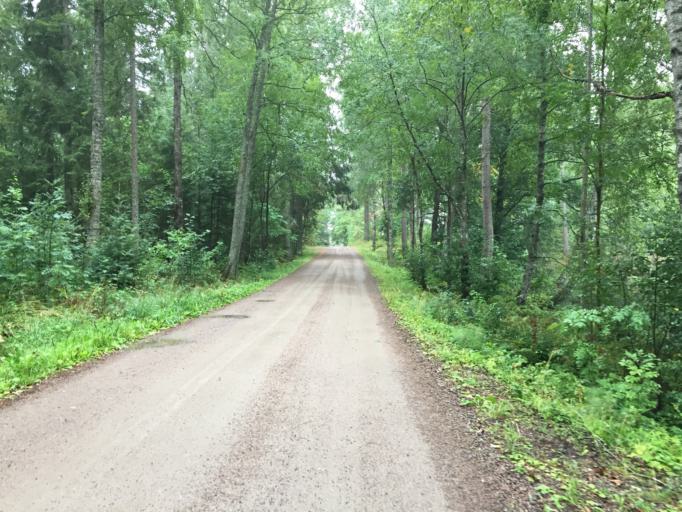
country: NO
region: Akershus
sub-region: Baerum
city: Lysaker
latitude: 59.9739
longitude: 10.6320
